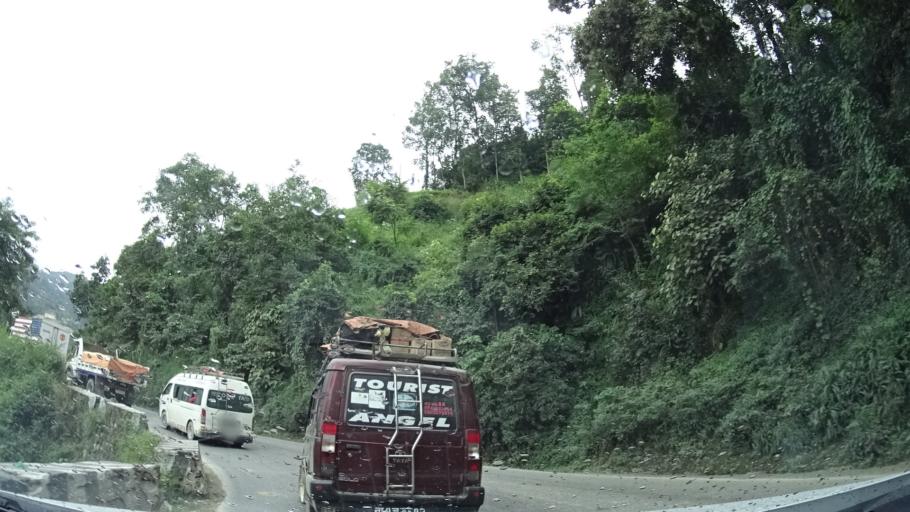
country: NP
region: Central Region
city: Kirtipur
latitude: 27.7118
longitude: 85.1881
